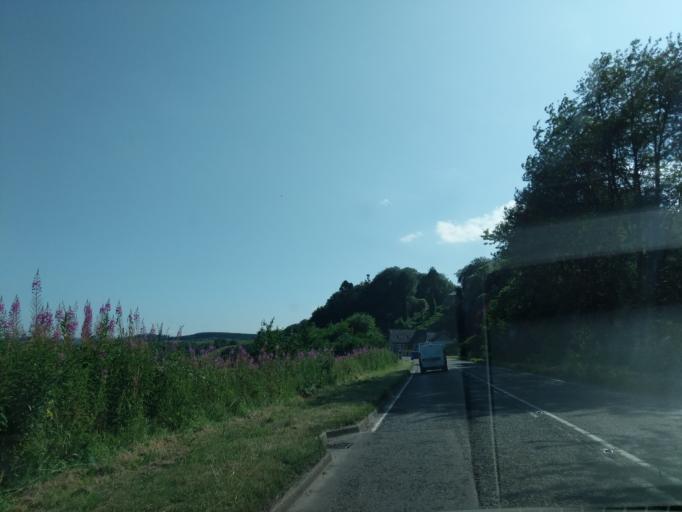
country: GB
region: Scotland
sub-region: Moray
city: Rothes
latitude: 57.5213
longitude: -3.2089
